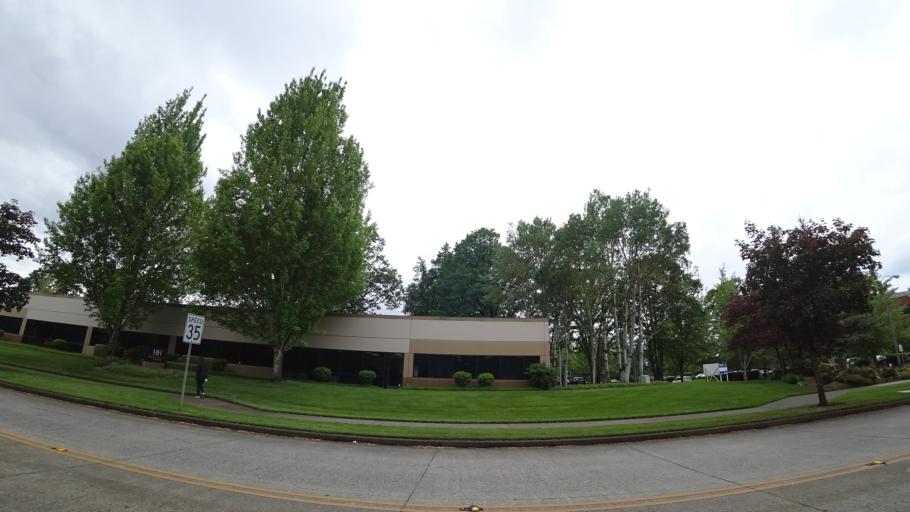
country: US
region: Oregon
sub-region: Washington County
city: Tigard
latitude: 45.4544
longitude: -122.7889
